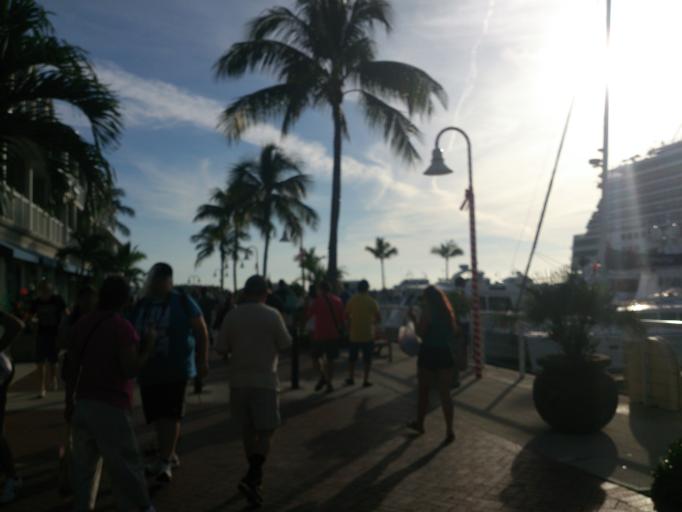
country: US
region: Florida
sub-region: Monroe County
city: Key West
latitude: 24.5580
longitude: -81.8077
